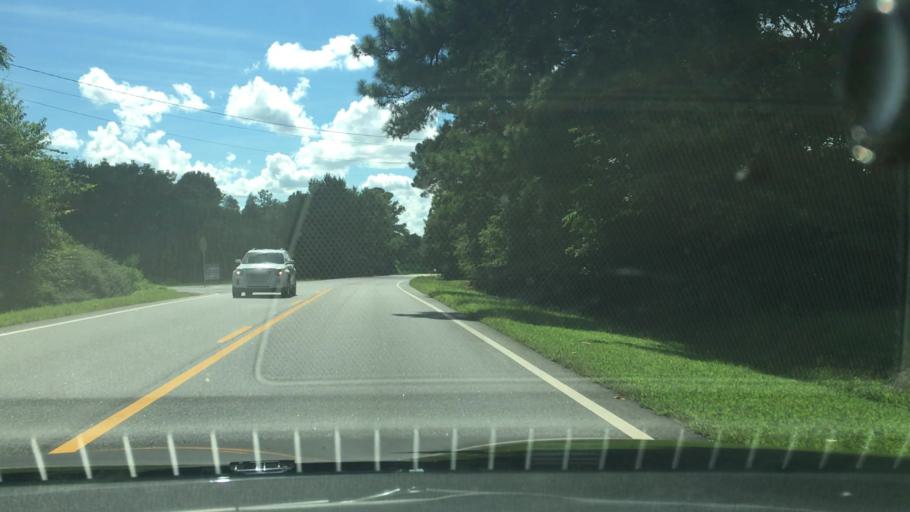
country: US
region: Georgia
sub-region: Butts County
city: Jackson
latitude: 33.2883
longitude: -83.9257
